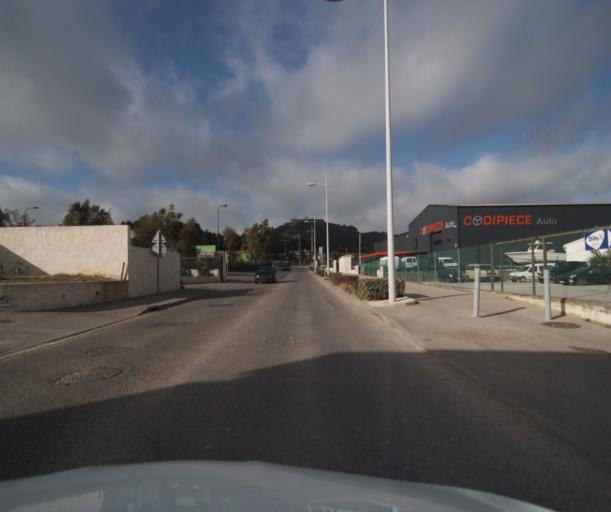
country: FR
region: Provence-Alpes-Cote d'Azur
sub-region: Departement du Var
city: Six-Fours-les-Plages
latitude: 43.1124
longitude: 5.8474
